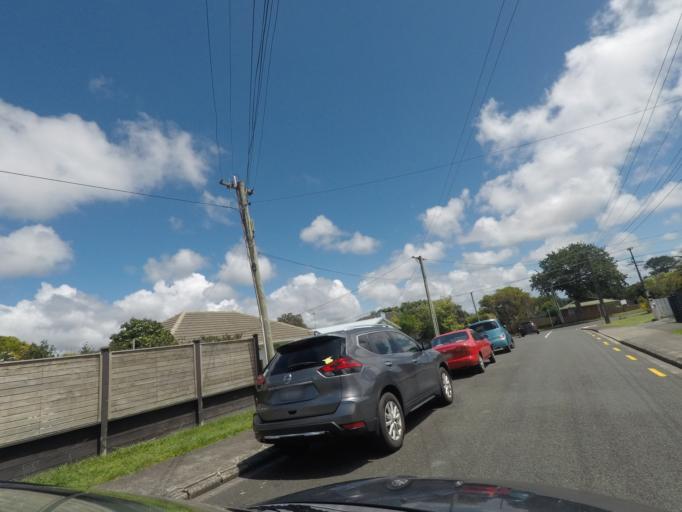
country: NZ
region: Auckland
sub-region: Auckland
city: Rosebank
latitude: -36.8800
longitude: 174.6417
